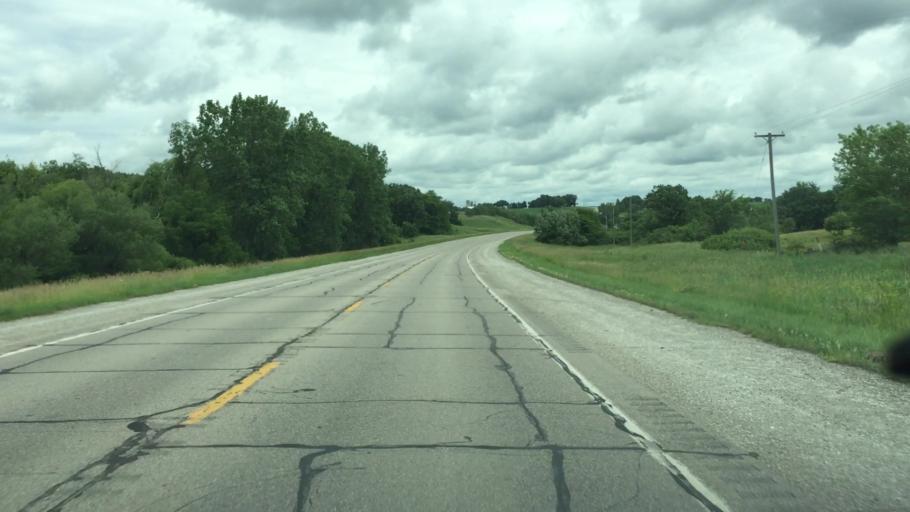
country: US
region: Iowa
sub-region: Jasper County
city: Monroe
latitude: 41.5333
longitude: -93.1018
